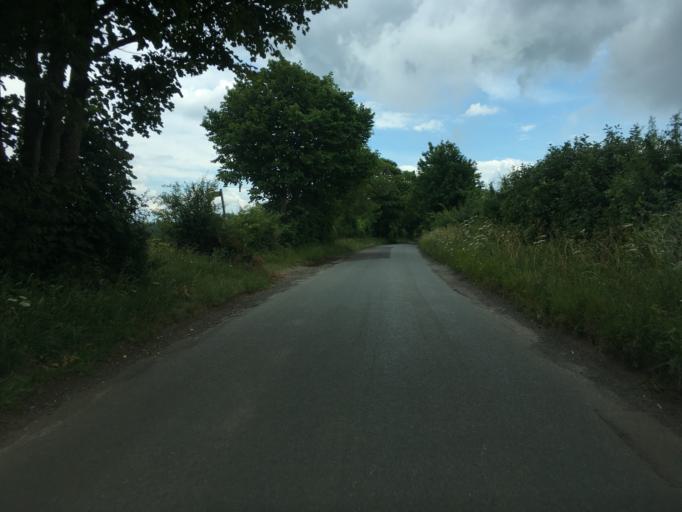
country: GB
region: England
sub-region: Gloucestershire
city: Coates
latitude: 51.7549
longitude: -2.0578
